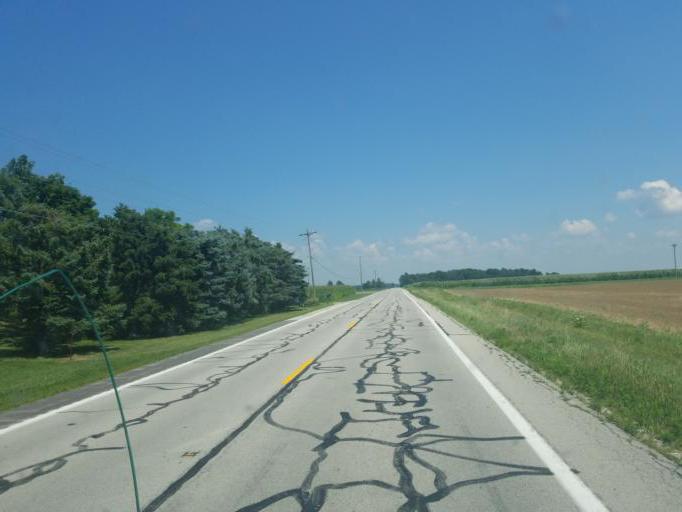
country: US
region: Ohio
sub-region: Shelby County
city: Jackson Center
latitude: 40.3960
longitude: -84.0710
